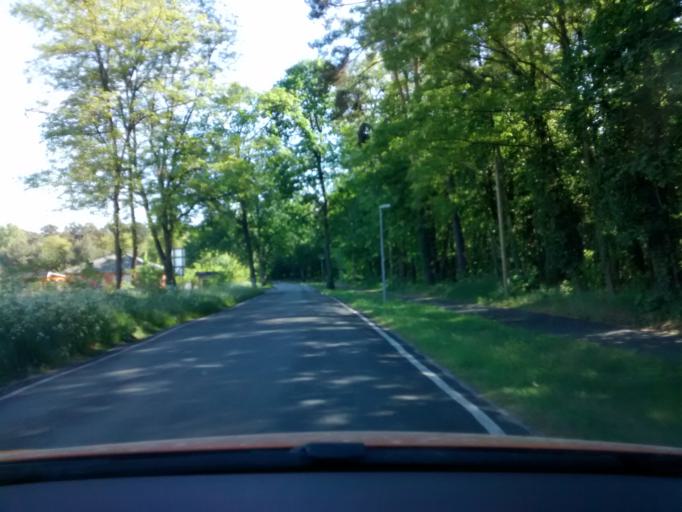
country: DE
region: Brandenburg
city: Bad Saarow
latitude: 52.2771
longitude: 14.0648
